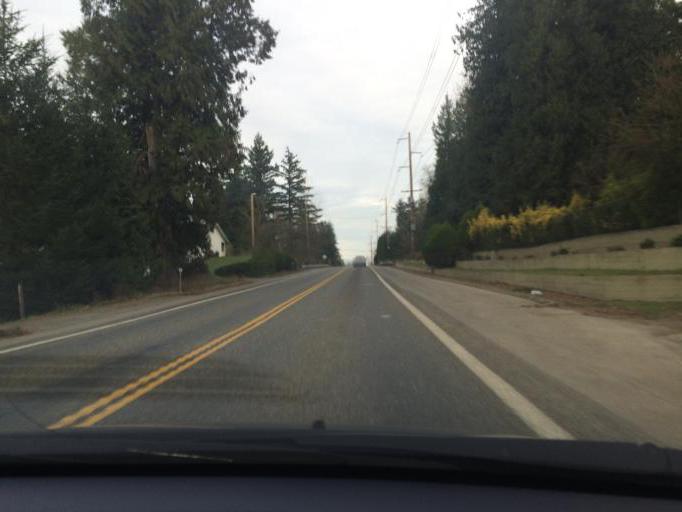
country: US
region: Washington
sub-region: Whatcom County
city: Lynden
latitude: 48.9353
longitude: -122.5363
